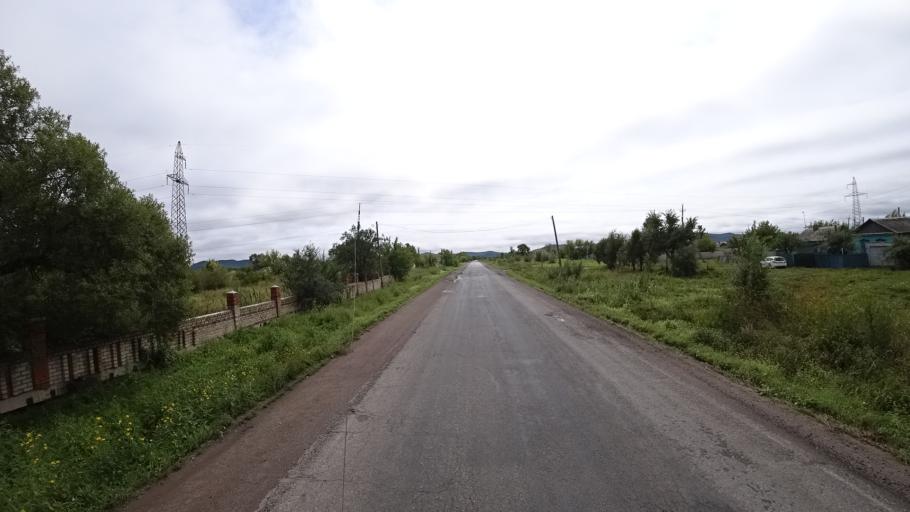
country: RU
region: Primorskiy
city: Monastyrishche
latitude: 44.2015
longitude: 132.4758
